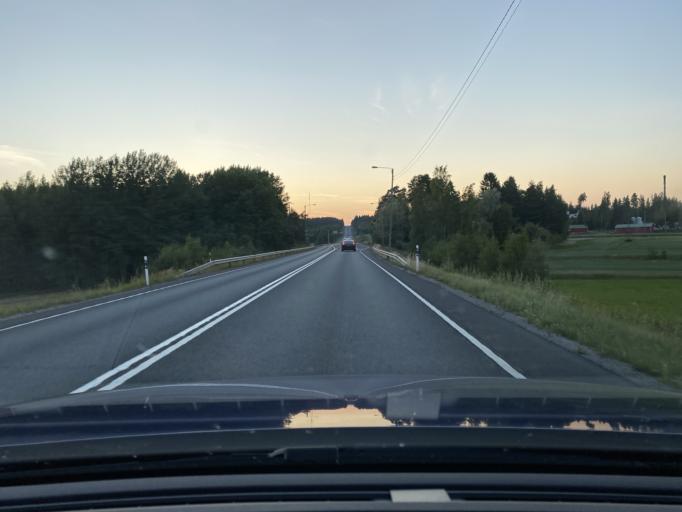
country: FI
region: Pirkanmaa
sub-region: Luoteis-Pirkanmaa
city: Ikaalinen
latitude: 61.7722
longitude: 23.0115
